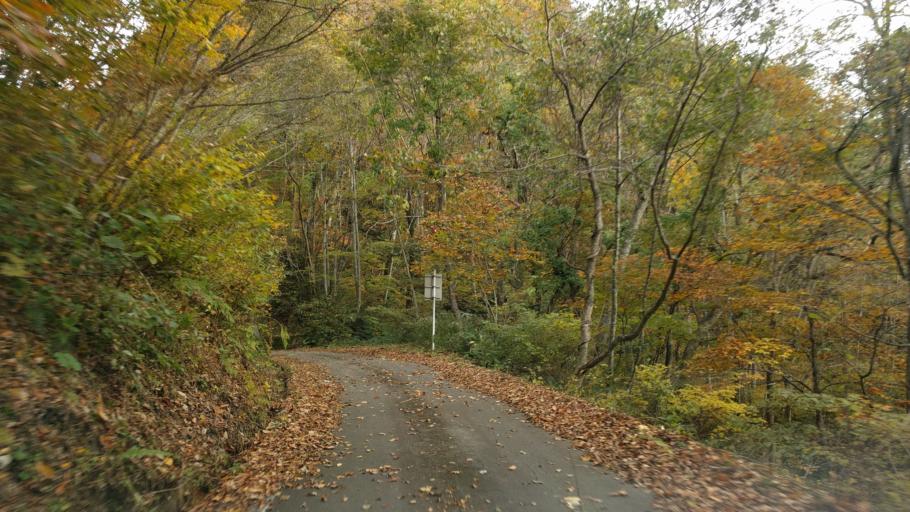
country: JP
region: Fukushima
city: Kitakata
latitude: 37.3905
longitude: 139.7148
